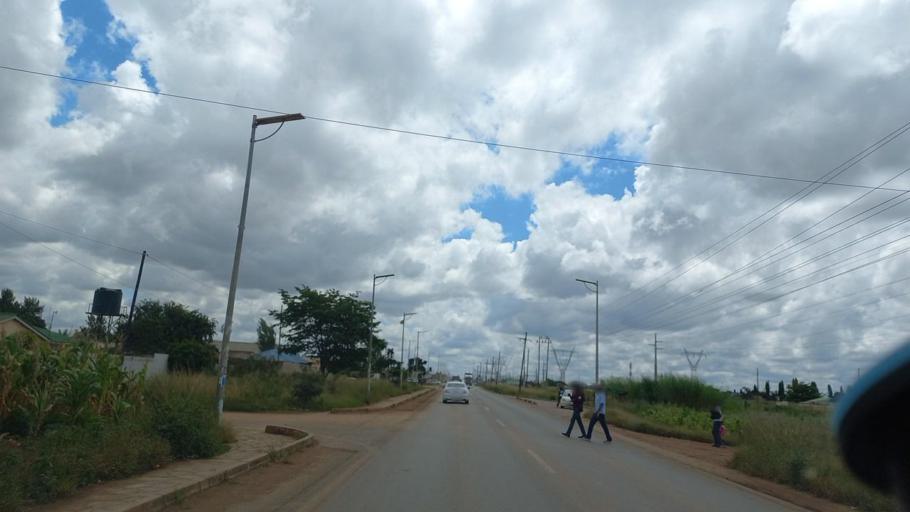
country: ZM
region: Lusaka
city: Lusaka
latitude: -15.4544
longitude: 28.3236
